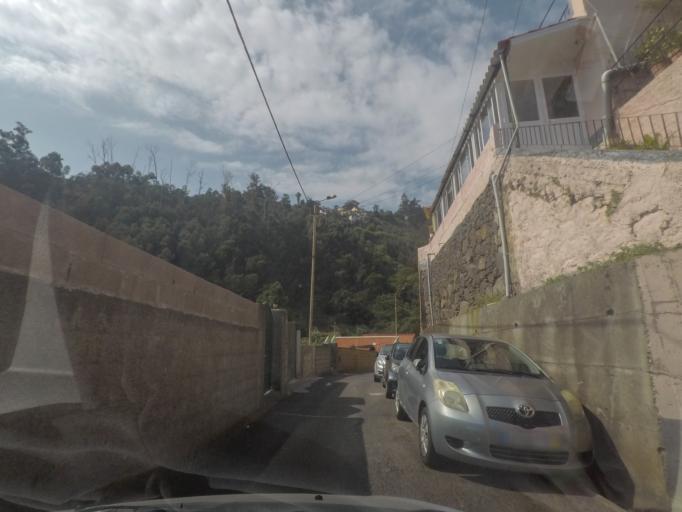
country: PT
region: Madeira
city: Camara de Lobos
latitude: 32.6732
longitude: -16.9518
